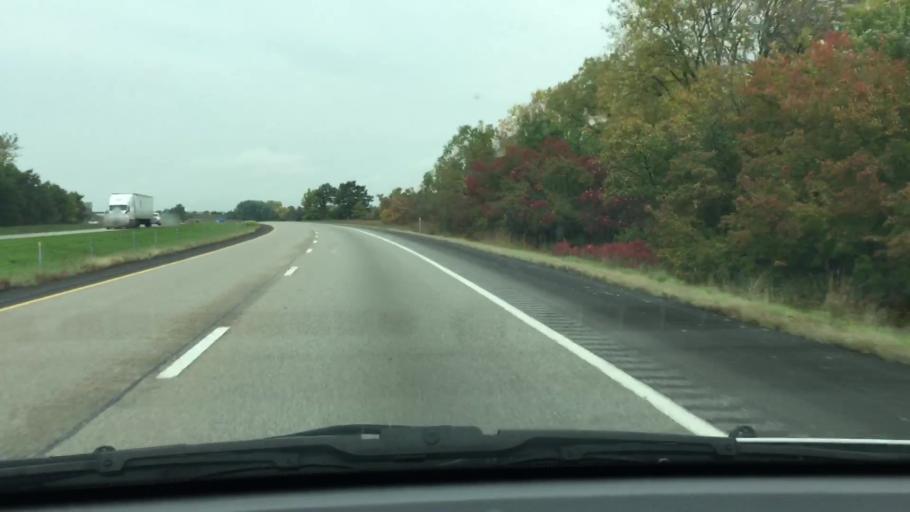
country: US
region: Iowa
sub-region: Muscatine County
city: West Liberty
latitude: 41.6566
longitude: -91.1940
